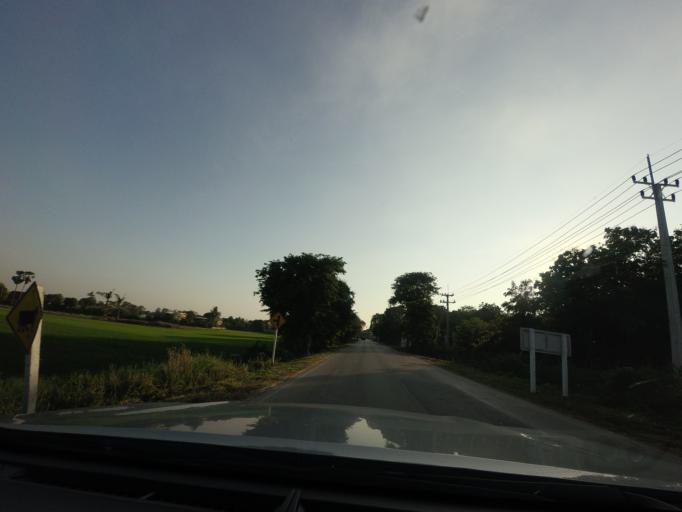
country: TH
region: Sukhothai
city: Sawankhalok
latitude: 17.3183
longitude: 99.8163
